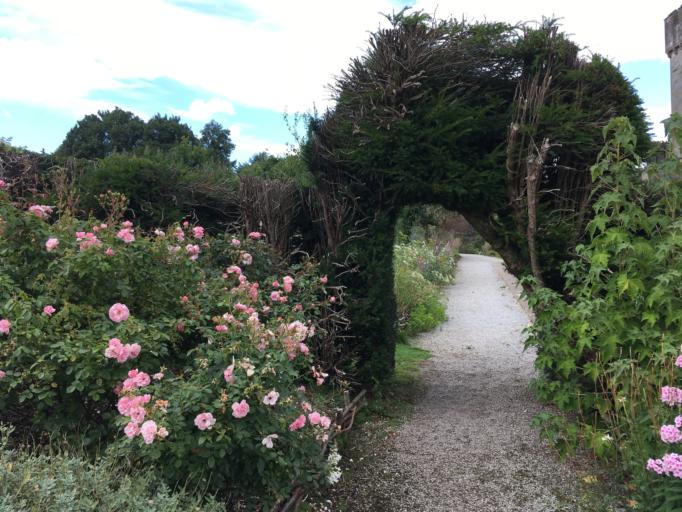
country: IE
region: Munster
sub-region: County Cork
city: Youghal
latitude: 52.1400
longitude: -7.9330
